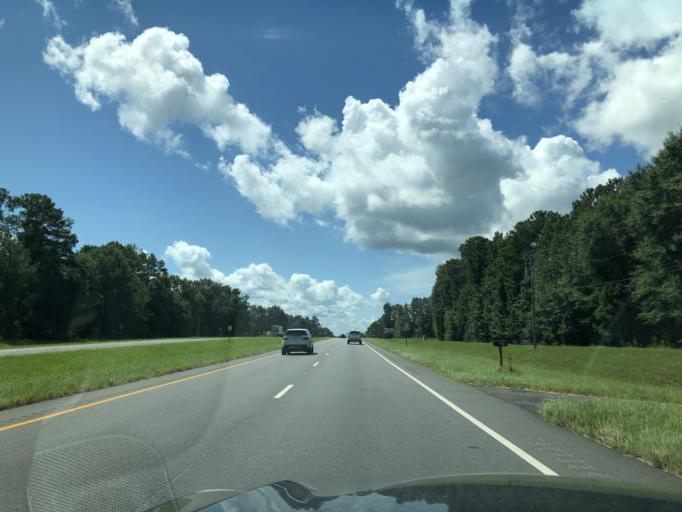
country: US
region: Alabama
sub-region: Barbour County
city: Eufaula
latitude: 32.0034
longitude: -85.1163
